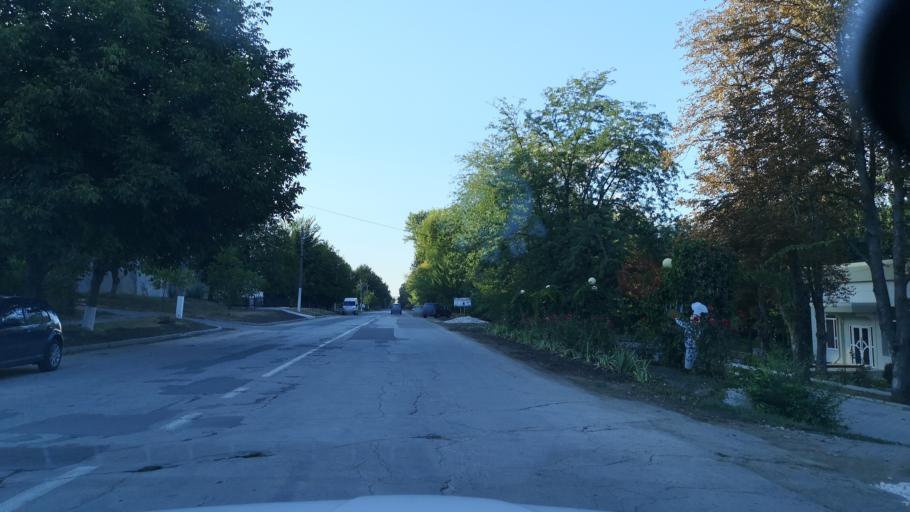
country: MD
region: Orhei
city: Orhei
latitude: 47.3907
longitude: 28.8231
